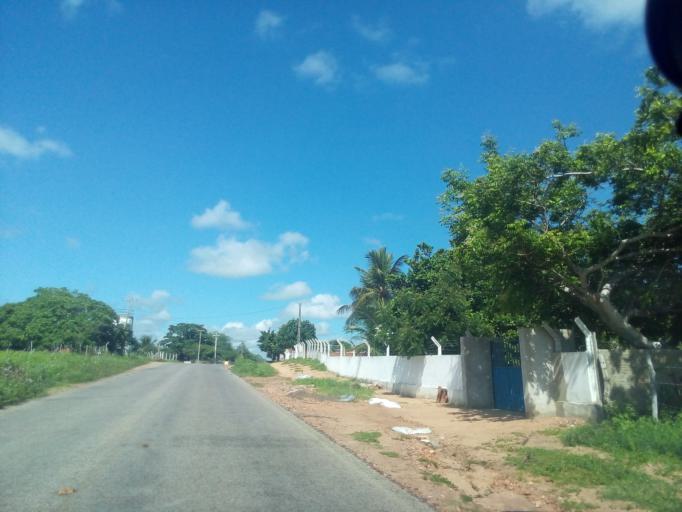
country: BR
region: Rio Grande do Norte
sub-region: Sao Paulo Do Potengi
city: Sao Paulo do Potengi
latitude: -5.9151
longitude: -35.7099
